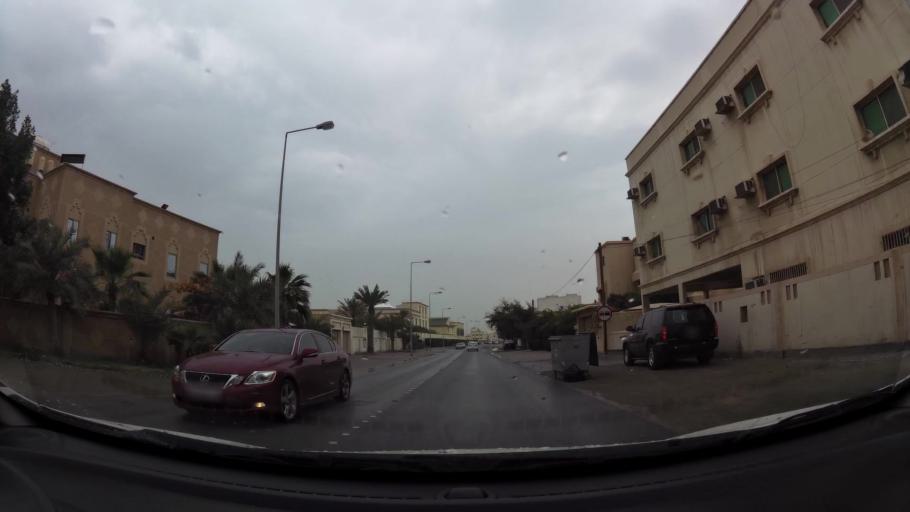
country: BH
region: Northern
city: Ar Rifa'
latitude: 26.1555
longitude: 50.5785
